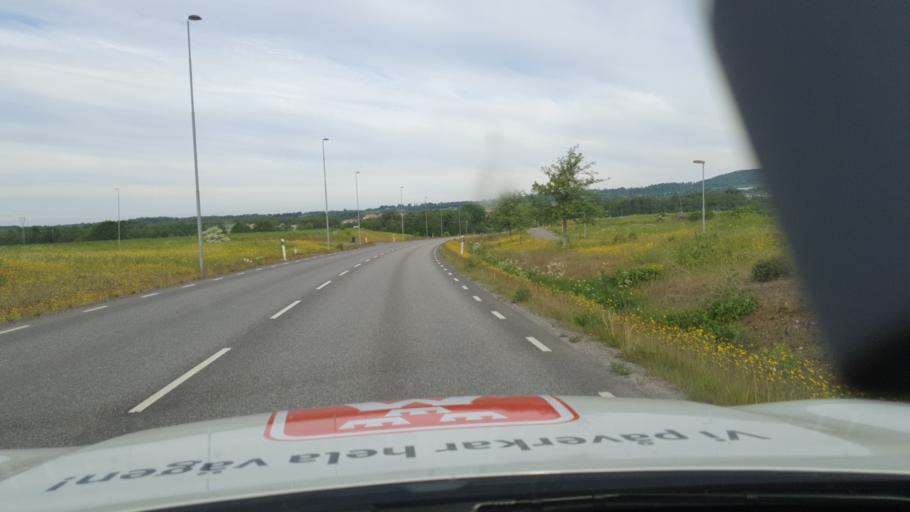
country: SE
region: Vaestra Goetaland
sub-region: Falkopings Kommun
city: Falkoeping
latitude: 58.1519
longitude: 13.5509
